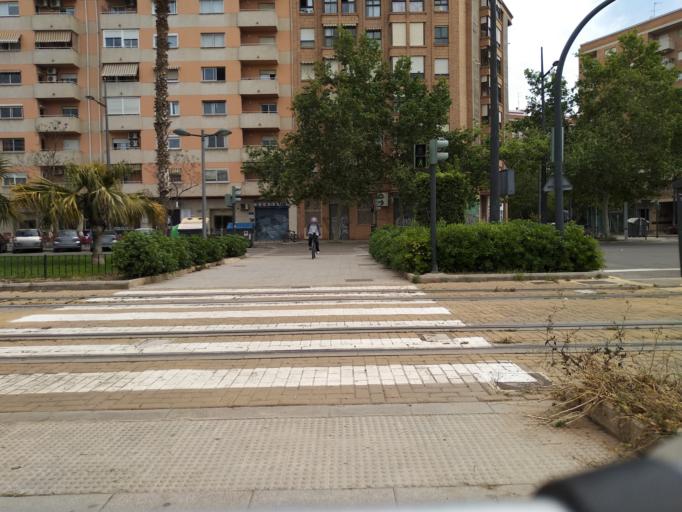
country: ES
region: Valencia
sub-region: Provincia de Valencia
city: Tavernes Blanques
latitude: 39.4874
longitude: -0.3694
